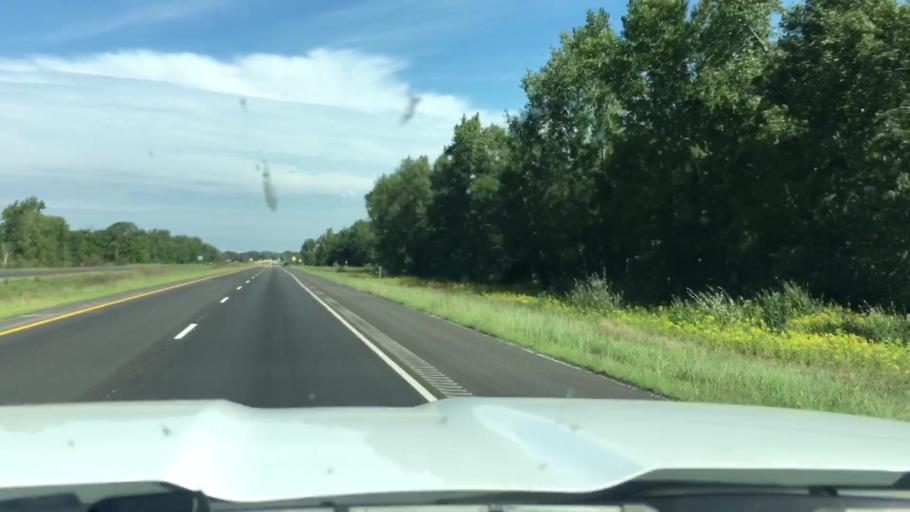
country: US
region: Michigan
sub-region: Saginaw County
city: Freeland
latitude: 43.5836
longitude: -84.1394
